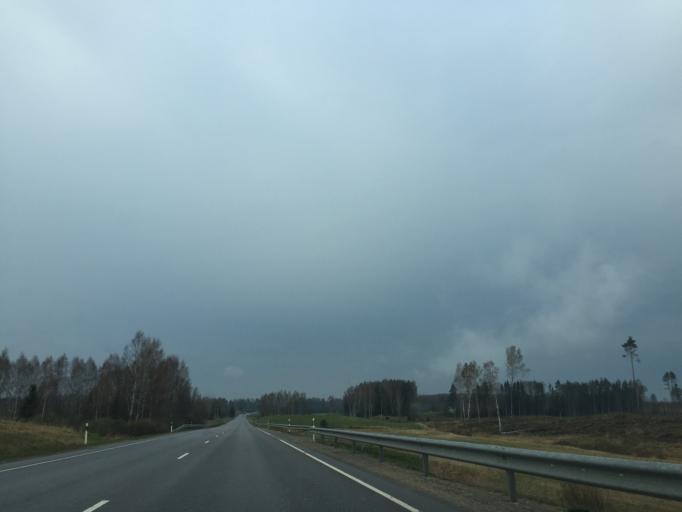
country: EE
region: Tartu
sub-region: UElenurme vald
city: Ulenurme
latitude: 58.1645
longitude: 26.6923
